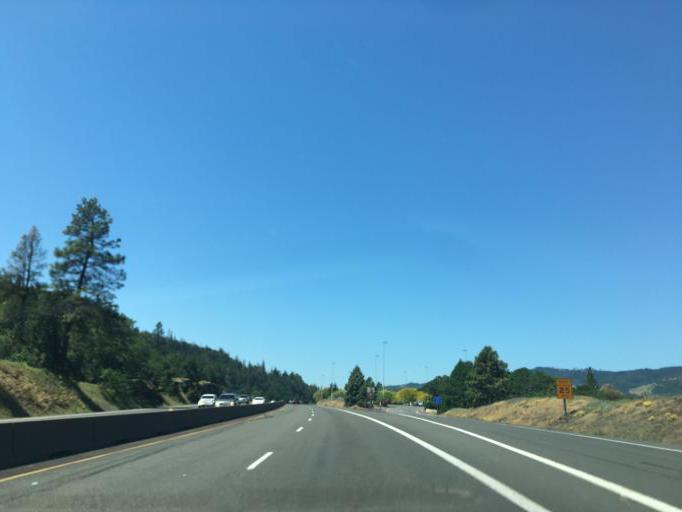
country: US
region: Oregon
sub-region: Wasco County
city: Chenoweth
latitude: 45.6952
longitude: -121.3358
